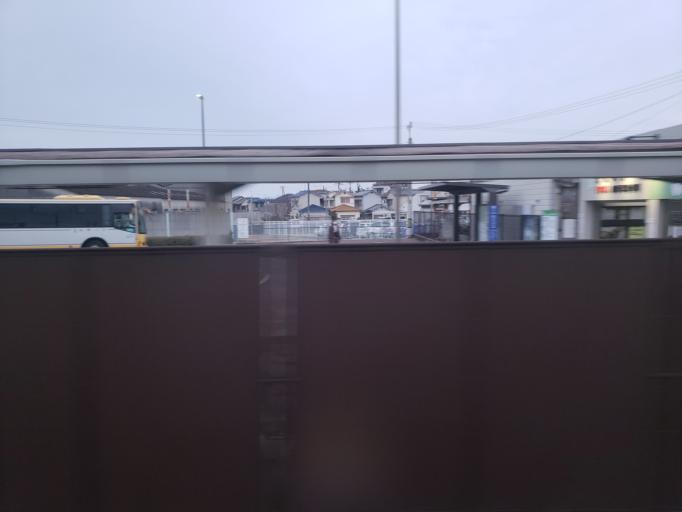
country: JP
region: Hyogo
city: Kakogawacho-honmachi
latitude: 34.7197
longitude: 134.8891
